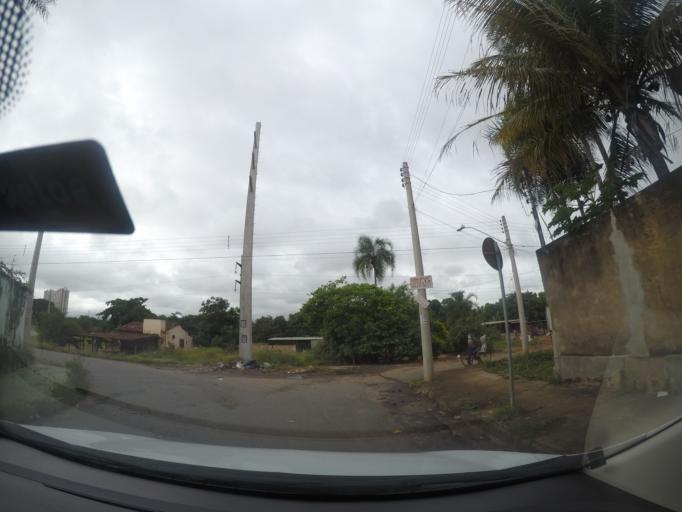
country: BR
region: Goias
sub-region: Goiania
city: Goiania
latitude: -16.7235
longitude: -49.2924
